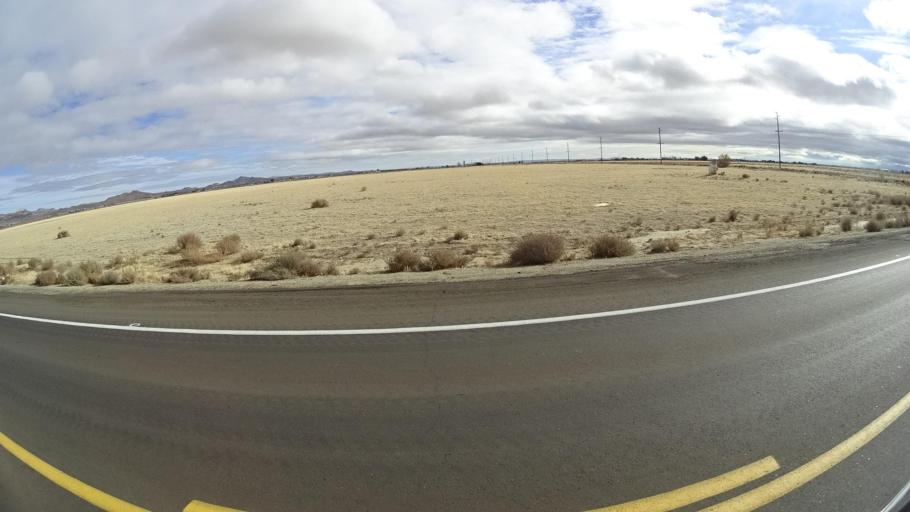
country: US
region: California
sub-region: Kern County
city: Rosamond
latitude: 34.8353
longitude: -118.2909
